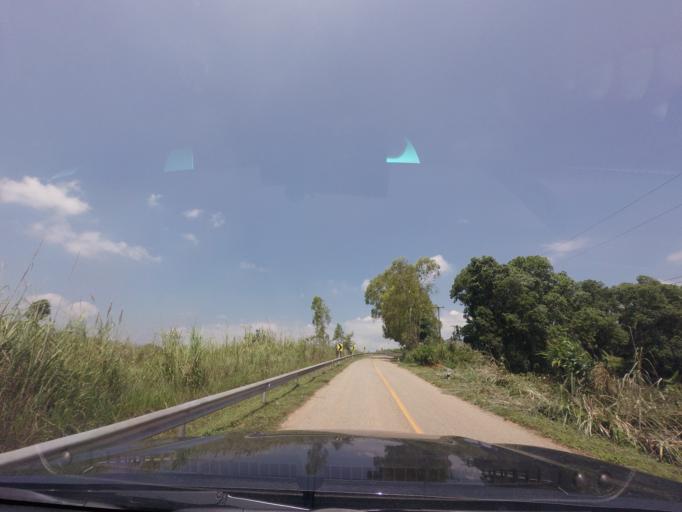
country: TH
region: Loei
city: Na Haeo
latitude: 17.5915
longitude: 100.9086
